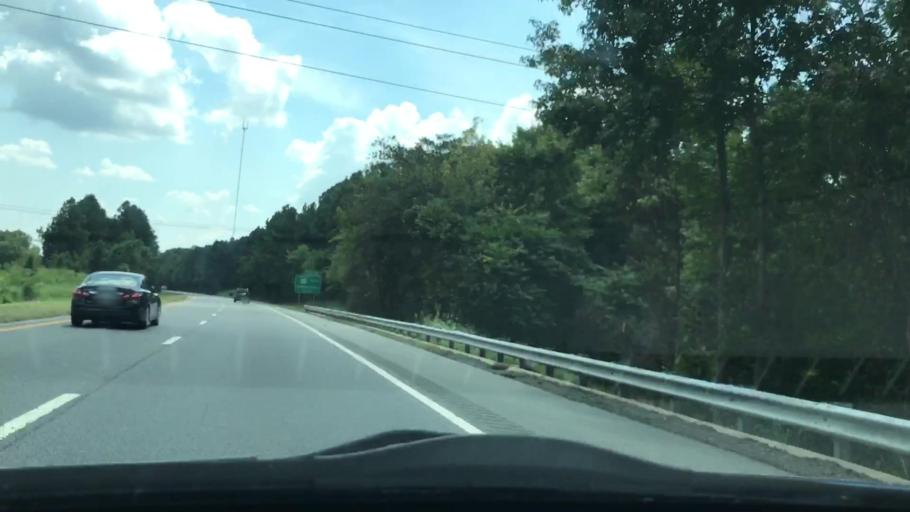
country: US
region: North Carolina
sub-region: Randolph County
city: Randleman
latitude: 35.8945
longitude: -79.8233
